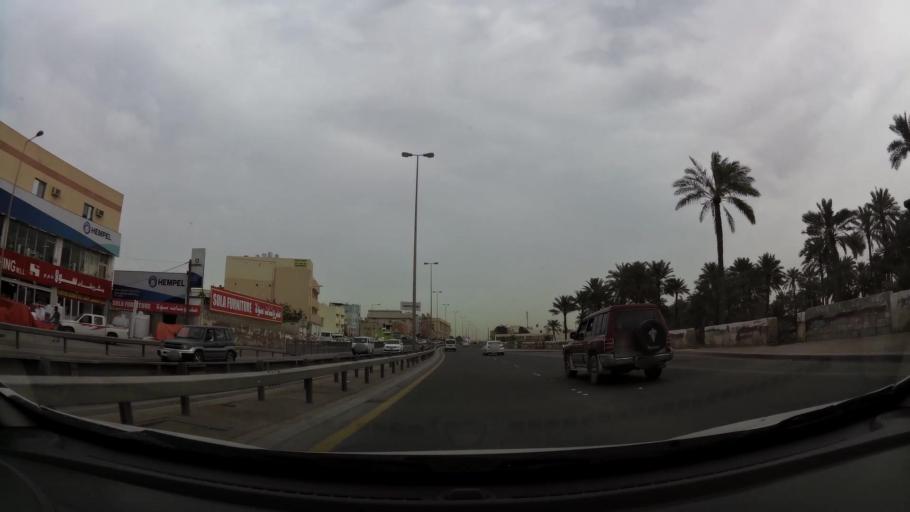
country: BH
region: Manama
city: Jidd Hafs
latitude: 26.2075
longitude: 50.5446
